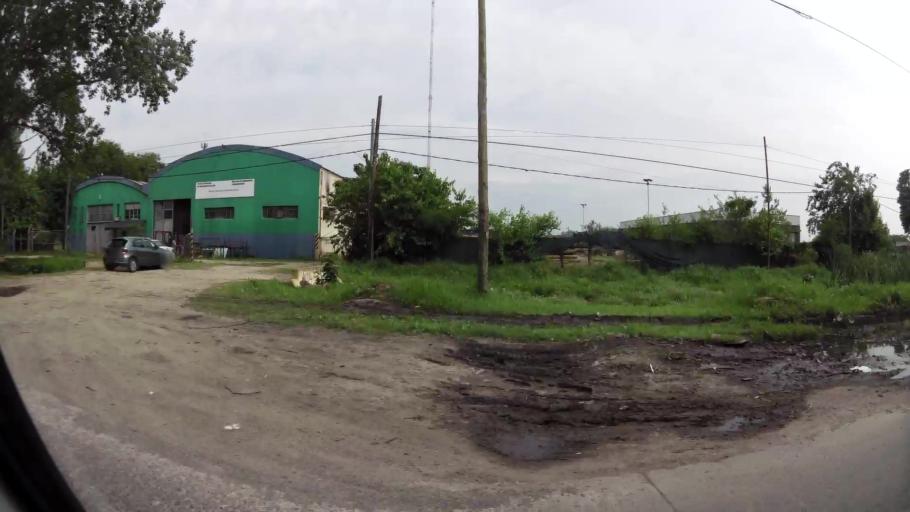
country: AR
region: Buenos Aires
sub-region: Partido de La Plata
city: La Plata
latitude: -34.9111
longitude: -58.0054
